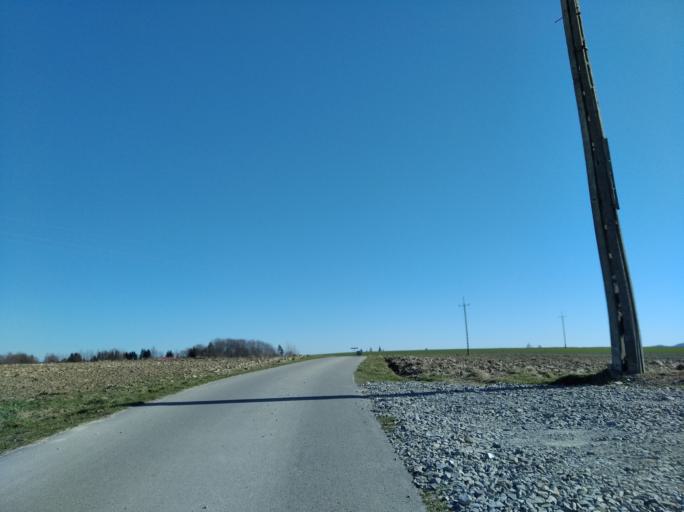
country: PL
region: Subcarpathian Voivodeship
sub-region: Powiat strzyzowski
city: Wisniowa
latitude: 49.9050
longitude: 21.7021
